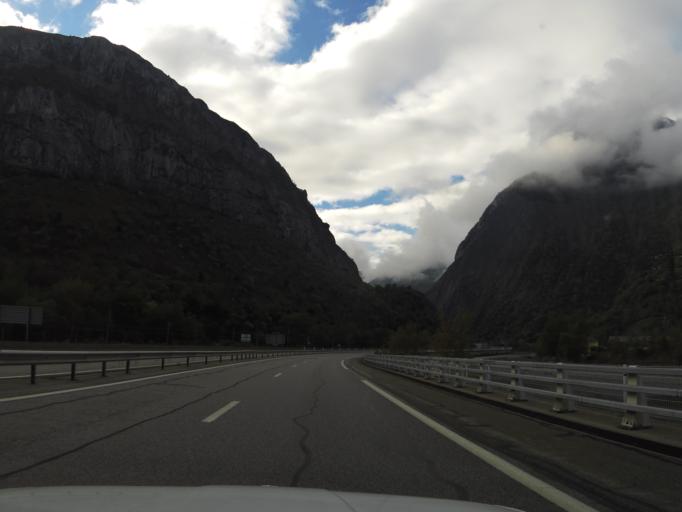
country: FR
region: Rhone-Alpes
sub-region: Departement de la Savoie
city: Saint-Michel-de-Maurienne
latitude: 45.2294
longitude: 6.4488
